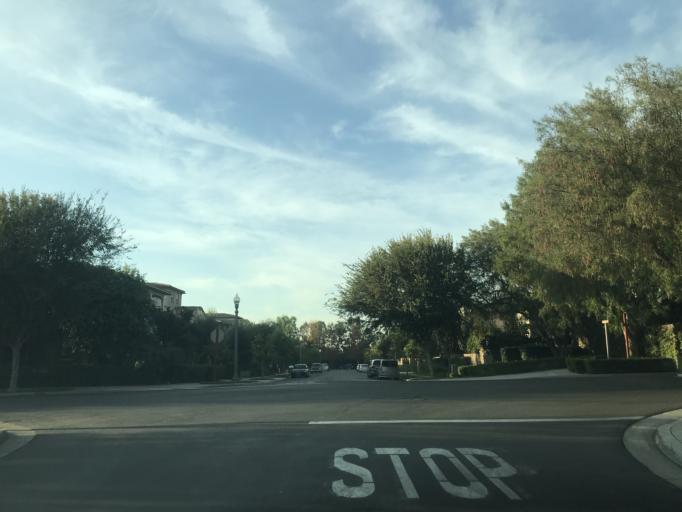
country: US
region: California
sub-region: Orange County
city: North Tustin
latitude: 33.7024
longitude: -117.7587
